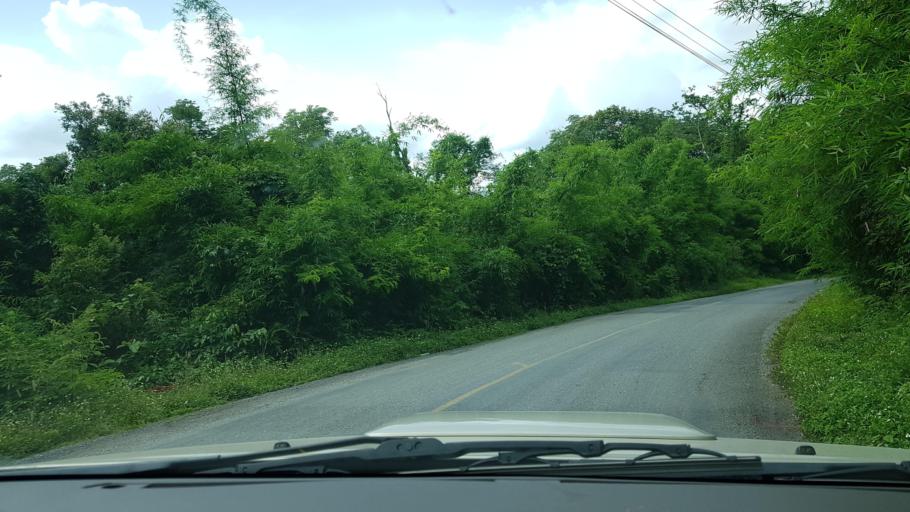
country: LA
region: Loungnamtha
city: Muang Nale
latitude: 20.1672
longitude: 101.5093
